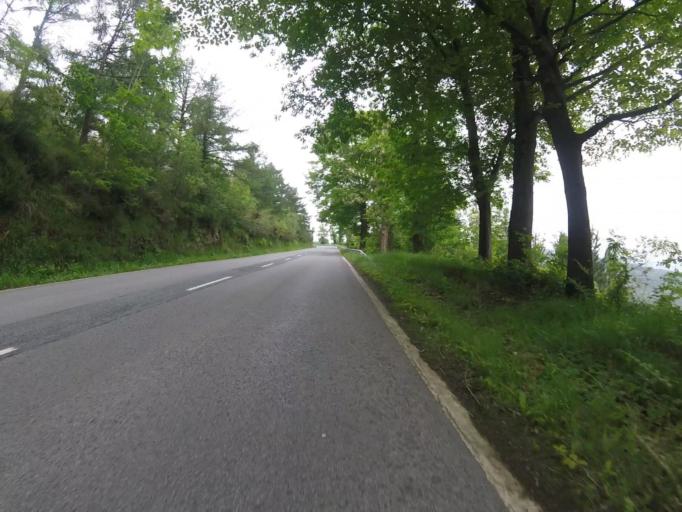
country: ES
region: Navarre
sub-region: Provincia de Navarra
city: Zugarramurdi
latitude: 43.2611
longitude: -1.4886
